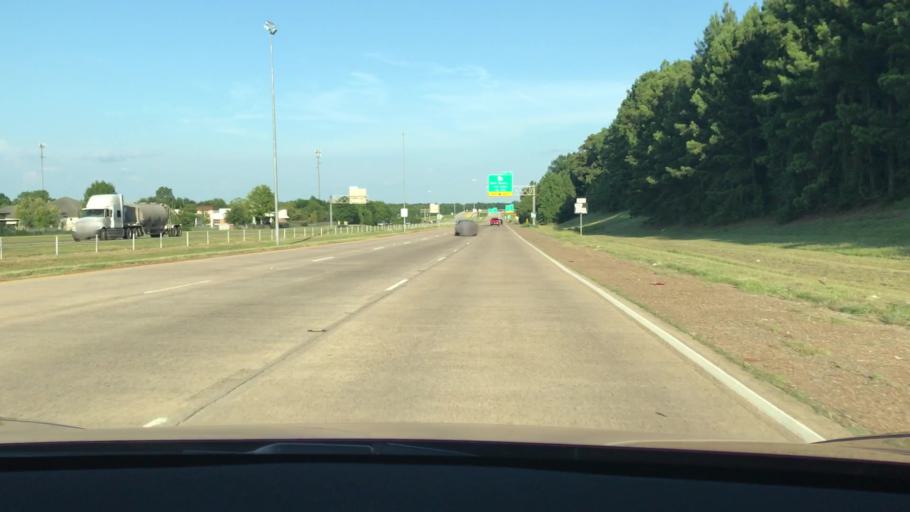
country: US
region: Louisiana
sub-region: Bossier Parish
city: Bossier City
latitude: 32.4145
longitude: -93.7338
